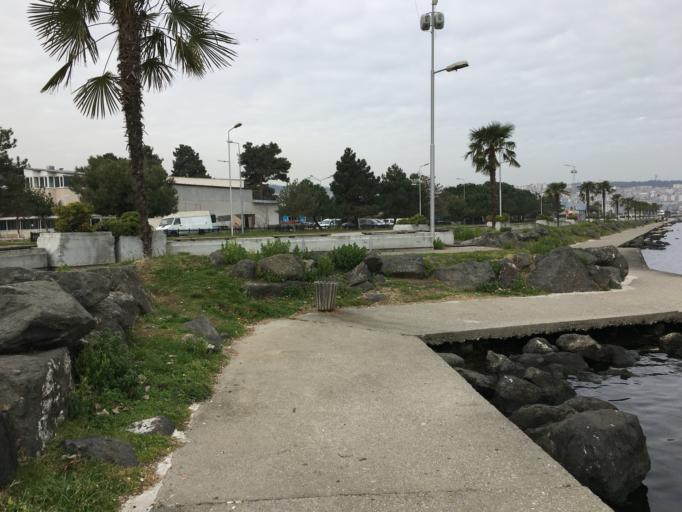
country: TR
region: Samsun
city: Samsun
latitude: 41.2907
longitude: 36.3420
